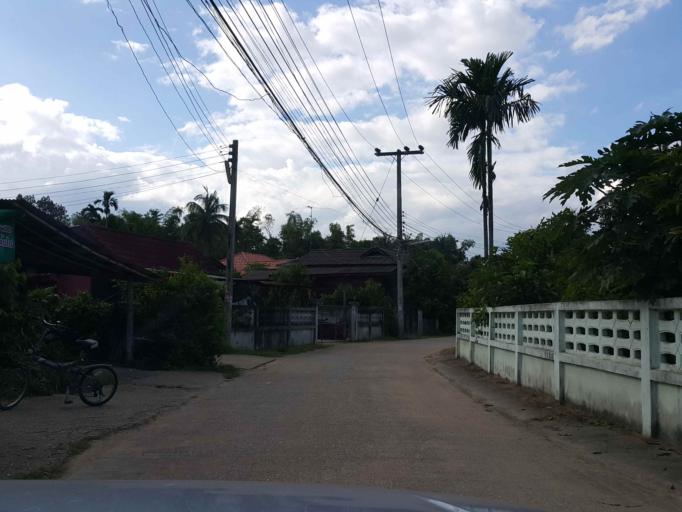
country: TH
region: Chiang Mai
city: Mae Taeng
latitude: 18.9711
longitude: 98.9158
